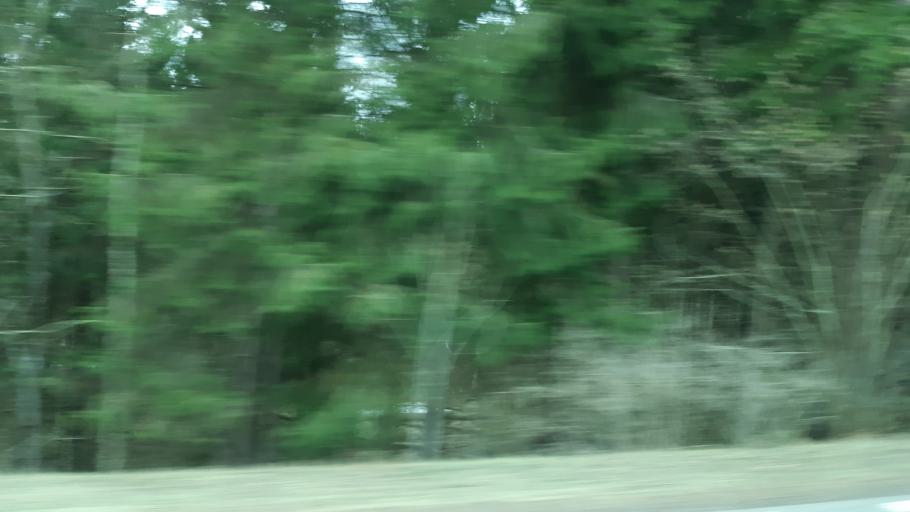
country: PL
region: Podlasie
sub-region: Suwalki
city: Suwalki
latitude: 54.3025
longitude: 22.9580
